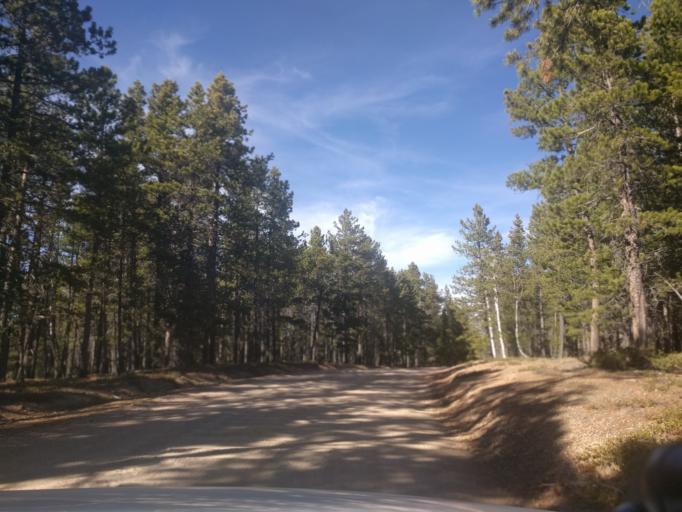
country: US
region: Colorado
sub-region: Douglas County
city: Perry Park
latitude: 39.1917
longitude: -105.0518
